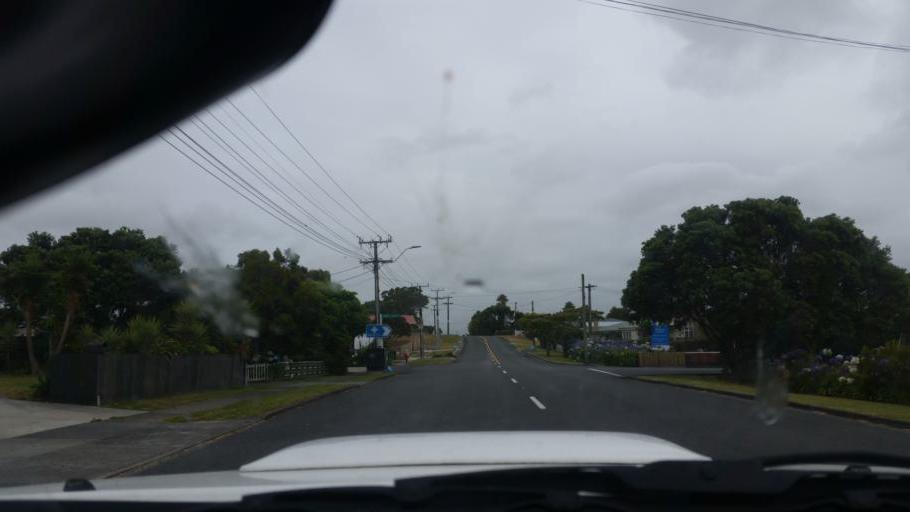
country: NZ
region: Northland
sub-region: Kaipara District
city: Dargaville
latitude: -35.9313
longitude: 173.8712
